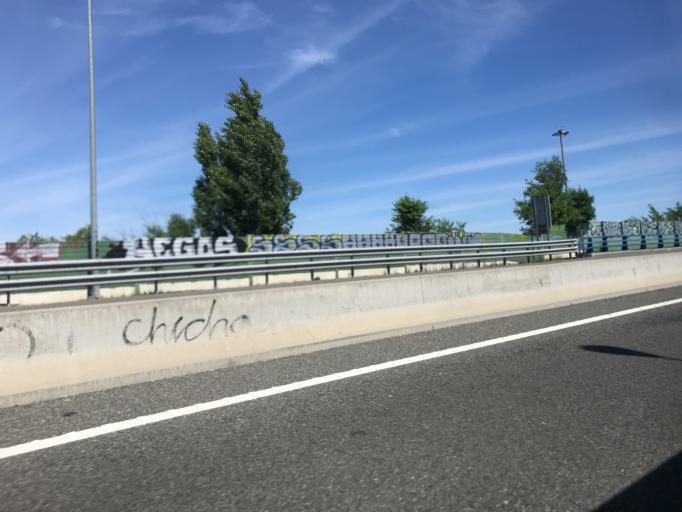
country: ES
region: Madrid
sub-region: Provincia de Madrid
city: San Blas
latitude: 40.4479
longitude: -3.5894
